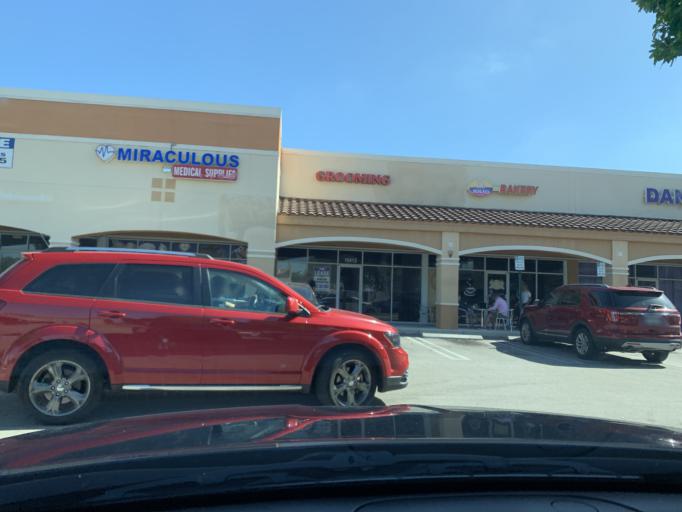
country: US
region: Florida
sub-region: Miami-Dade County
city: Country Walk
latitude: 25.6242
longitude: -80.4133
